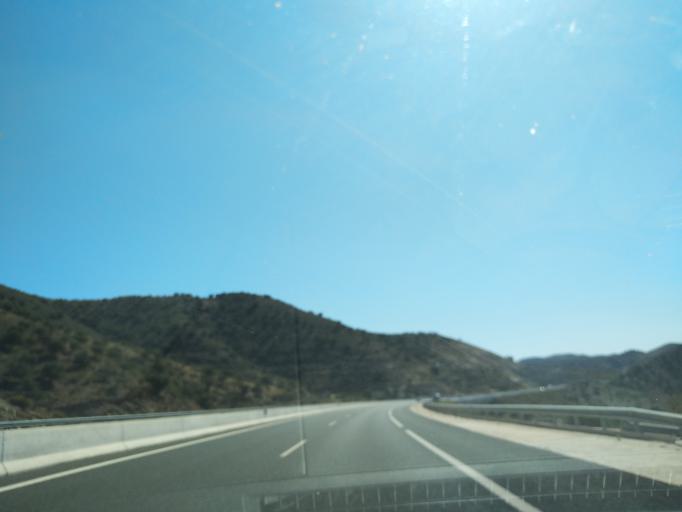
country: ES
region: Andalusia
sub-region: Provincia de Malaga
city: Almogia
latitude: 36.8333
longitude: -4.4731
